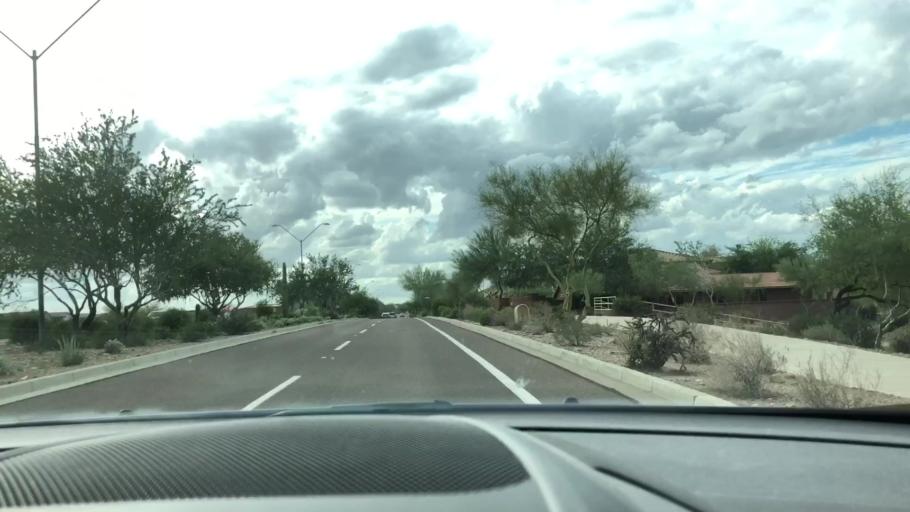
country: US
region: Arizona
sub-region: Maricopa County
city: Sun City West
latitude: 33.7291
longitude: -112.2457
